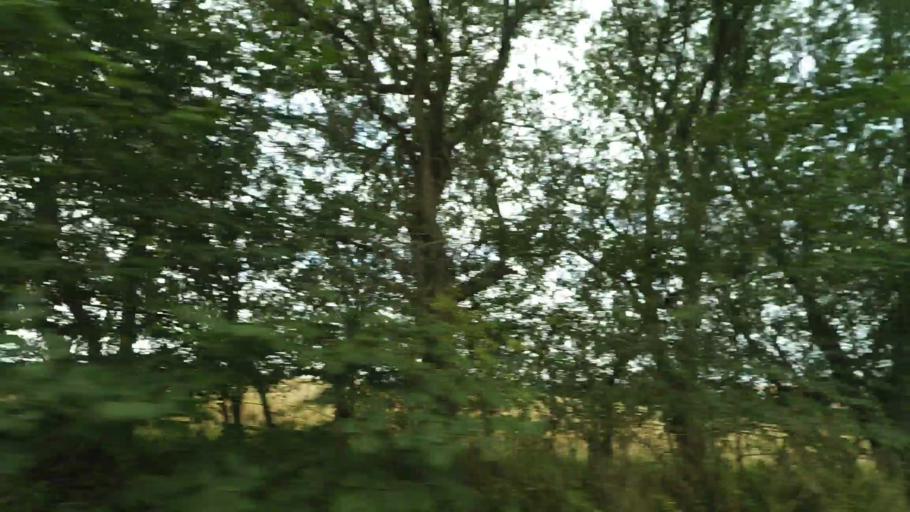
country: DK
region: Central Jutland
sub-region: Syddjurs Kommune
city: Ronde
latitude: 56.3385
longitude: 10.4686
